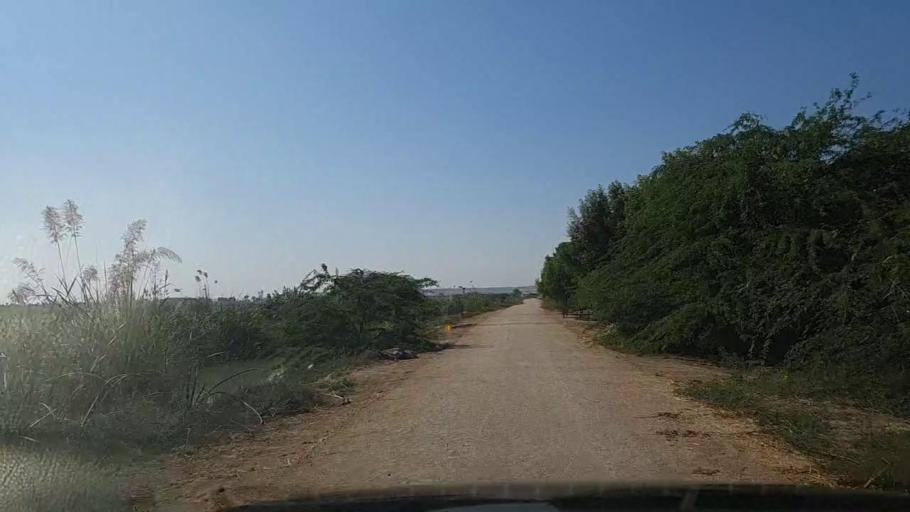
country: PK
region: Sindh
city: Thatta
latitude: 24.6347
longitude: 67.8739
